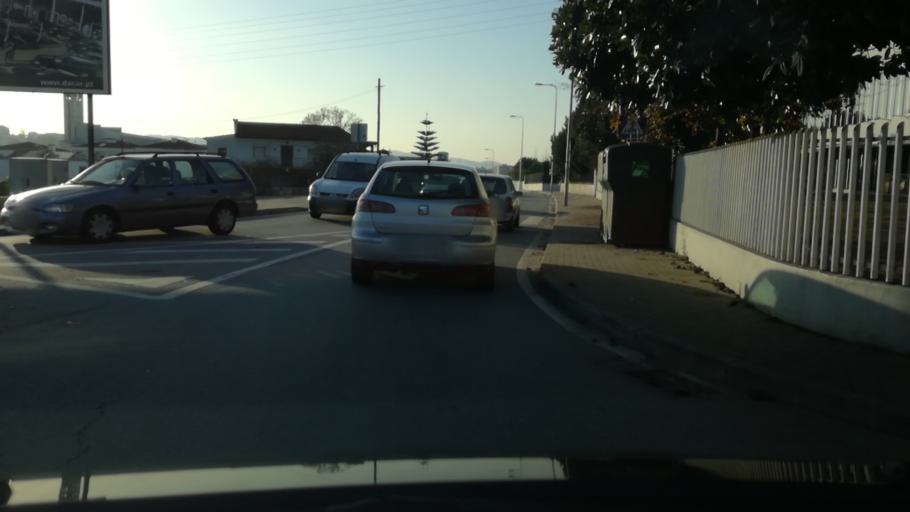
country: PT
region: Porto
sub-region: Trofa
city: Bougado
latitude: 41.3404
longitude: -8.5436
